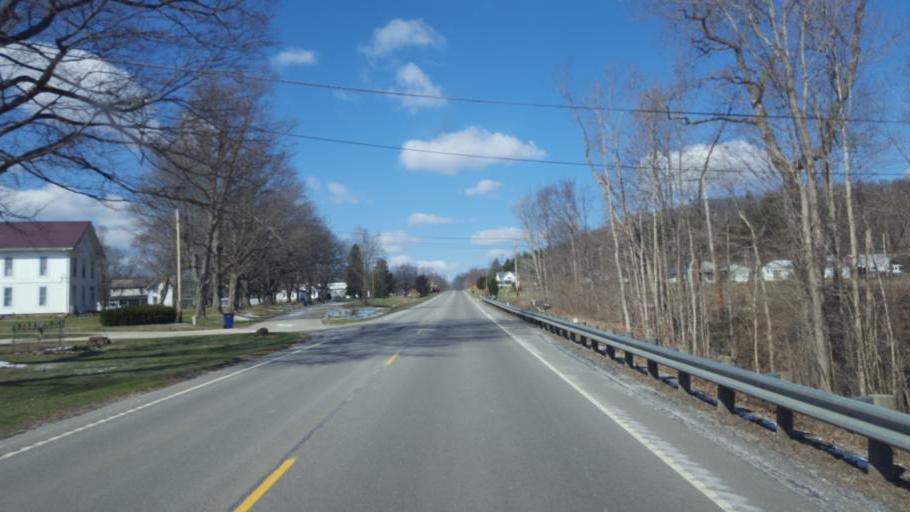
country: US
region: Ohio
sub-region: Licking County
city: Utica
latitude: 40.2304
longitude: -82.4601
